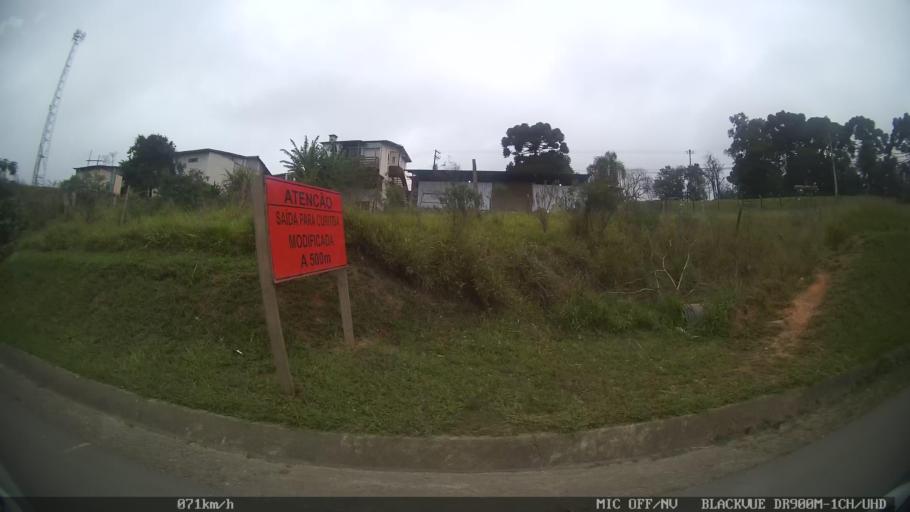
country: BR
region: Parana
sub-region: Almirante Tamandare
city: Almirante Tamandare
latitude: -25.3539
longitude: -49.2905
